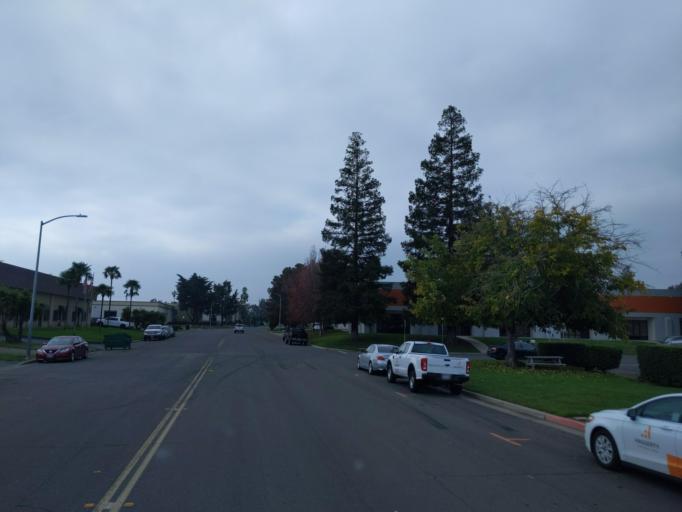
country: US
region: California
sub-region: San Joaquin County
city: August
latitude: 37.9851
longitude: -121.2544
